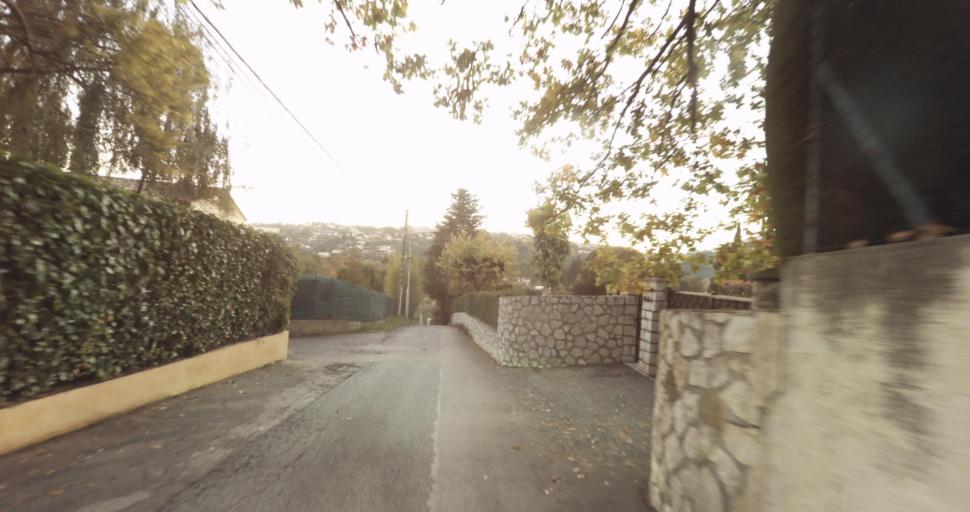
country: FR
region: Provence-Alpes-Cote d'Azur
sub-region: Departement des Alpes-Maritimes
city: Vence
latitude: 43.7273
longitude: 7.1307
